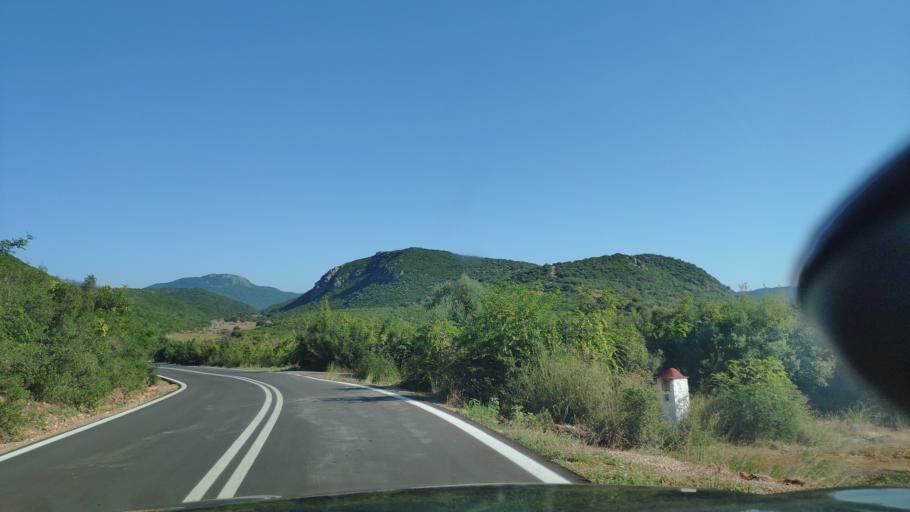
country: GR
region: West Greece
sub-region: Nomos Aitolias kai Akarnanias
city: Fitiai
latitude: 38.6667
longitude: 21.1435
